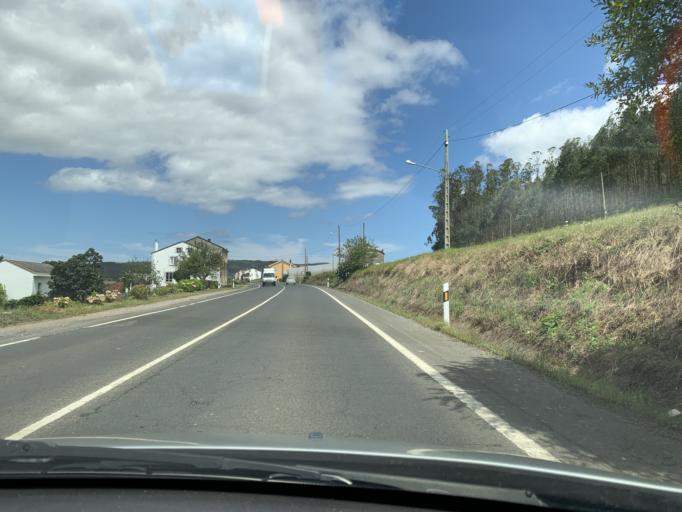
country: ES
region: Galicia
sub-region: Provincia de Lugo
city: Barreiros
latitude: 43.4931
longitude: -7.2765
